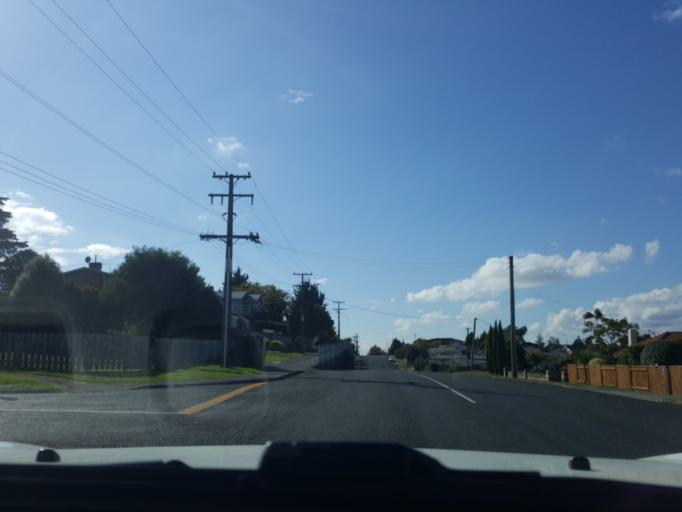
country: NZ
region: Waikato
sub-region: Waikato District
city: Ngaruawahia
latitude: -37.5459
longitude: 175.1687
